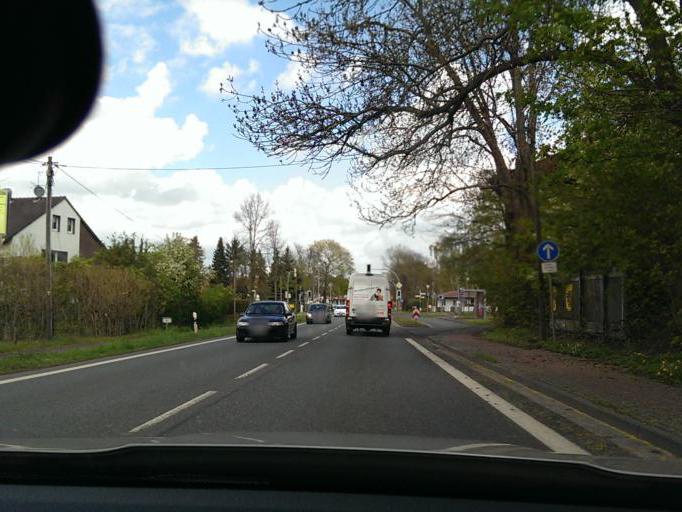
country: DE
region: Lower Saxony
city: Pattensen
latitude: 52.2734
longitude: 9.7936
